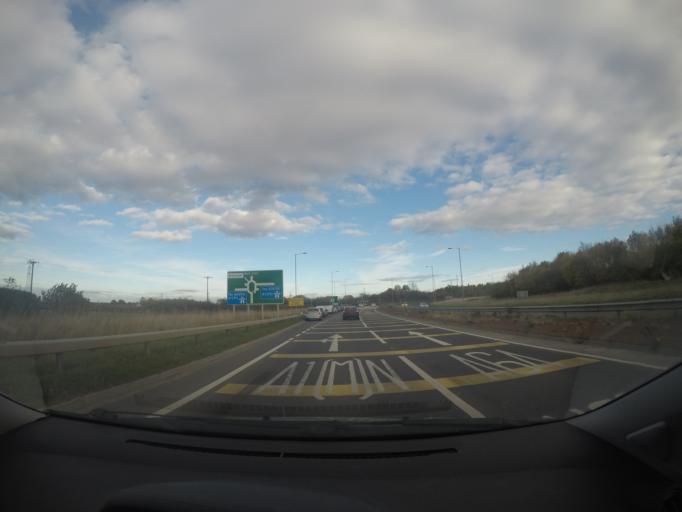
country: GB
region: England
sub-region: City and Borough of Leeds
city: Bramham
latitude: 53.8557
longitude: -1.3500
